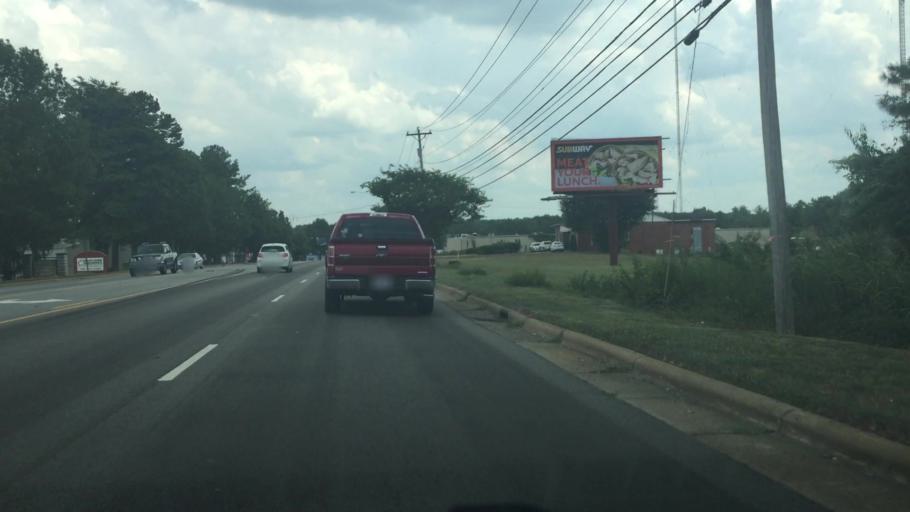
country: US
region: North Carolina
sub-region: Rowan County
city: Salisbury
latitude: 35.6807
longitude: -80.5063
